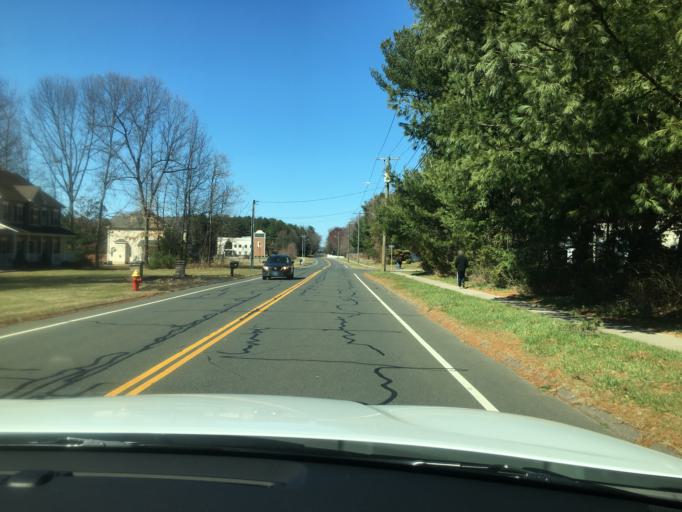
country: US
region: Connecticut
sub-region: Hartford County
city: East Hartford
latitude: 41.8026
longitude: -72.5834
